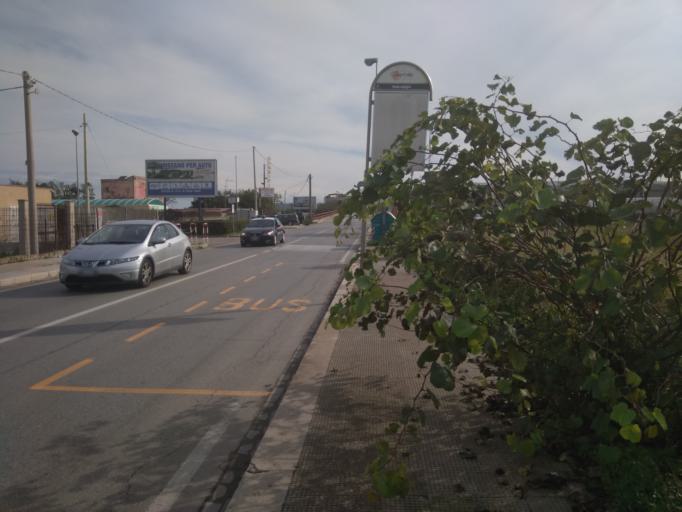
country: IT
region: Apulia
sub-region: Provincia di Bari
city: Bari
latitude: 41.1119
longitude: 16.9012
